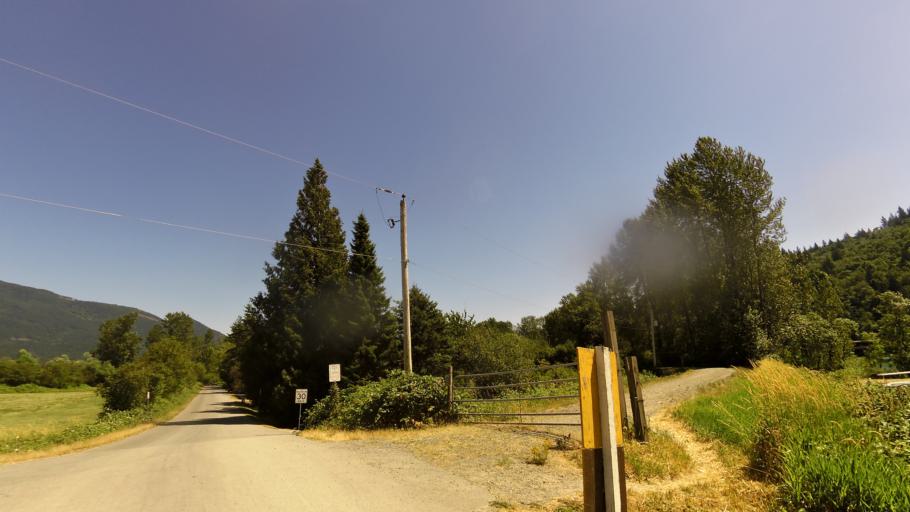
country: CA
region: British Columbia
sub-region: Fraser Valley Regional District
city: Chilliwack
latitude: 49.2369
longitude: -121.9619
